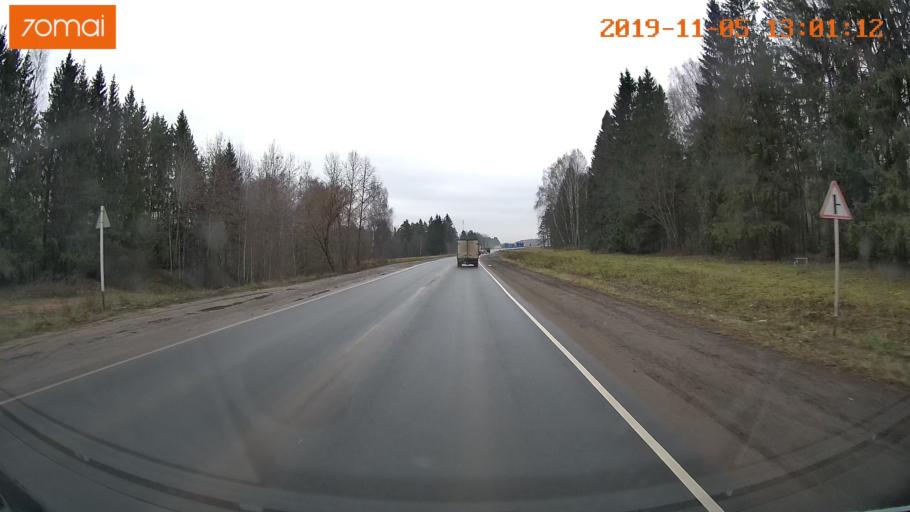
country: RU
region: Ivanovo
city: Kokhma
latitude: 56.9102
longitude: 41.1582
